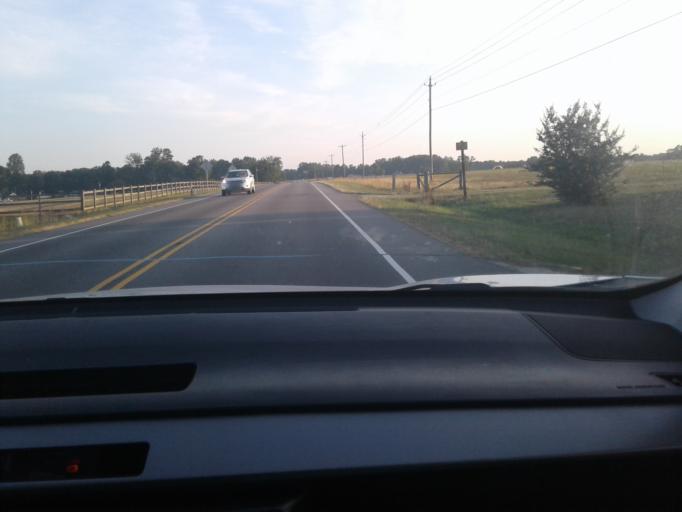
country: US
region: North Carolina
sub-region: Harnett County
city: Lillington
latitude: 35.4500
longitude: -78.8287
